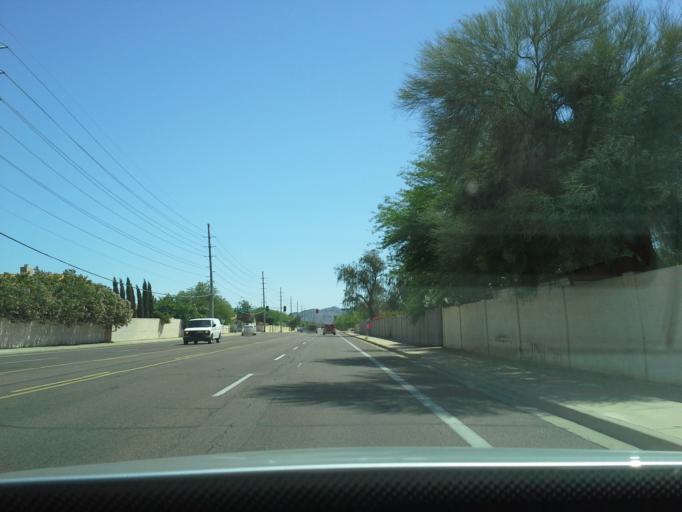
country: US
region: Arizona
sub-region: Maricopa County
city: Paradise Valley
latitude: 33.6348
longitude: -111.9603
